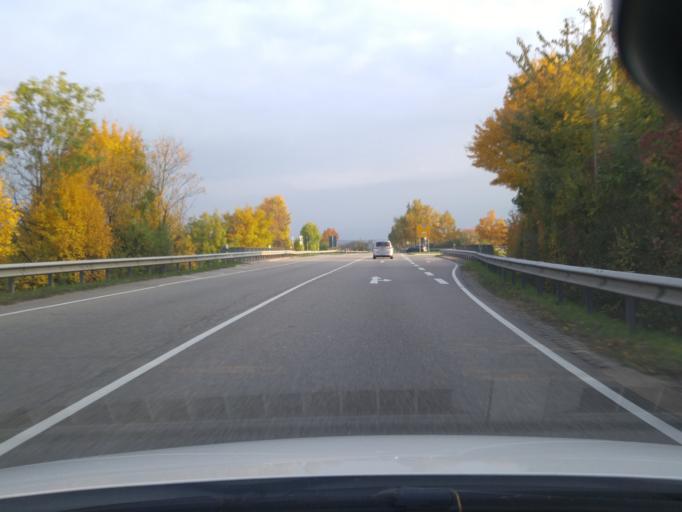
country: DE
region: Baden-Wuerttemberg
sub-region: Karlsruhe Region
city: Wiesloch
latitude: 49.2843
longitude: 8.6873
